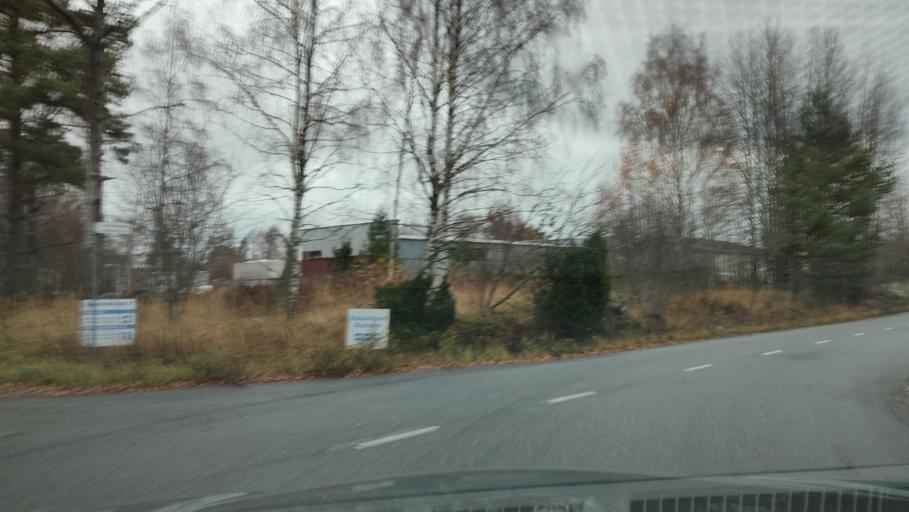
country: FI
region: Ostrobothnia
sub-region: Sydosterbotten
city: Kristinestad
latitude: 62.2772
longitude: 21.4002
